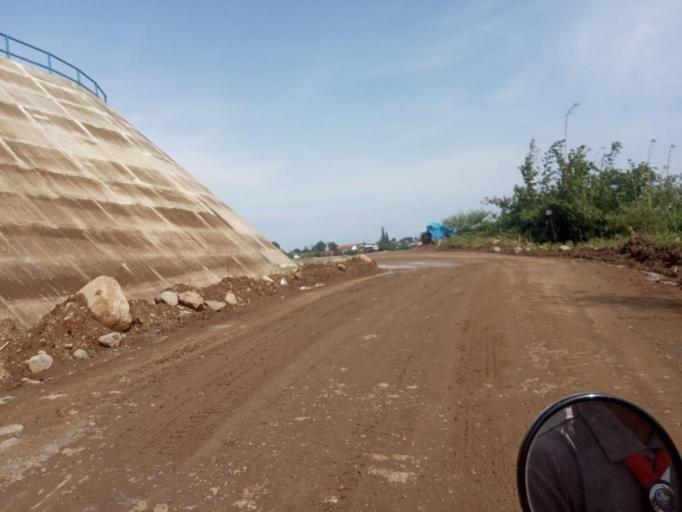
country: ID
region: West Java
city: Caringin
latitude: -6.6592
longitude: 106.8826
